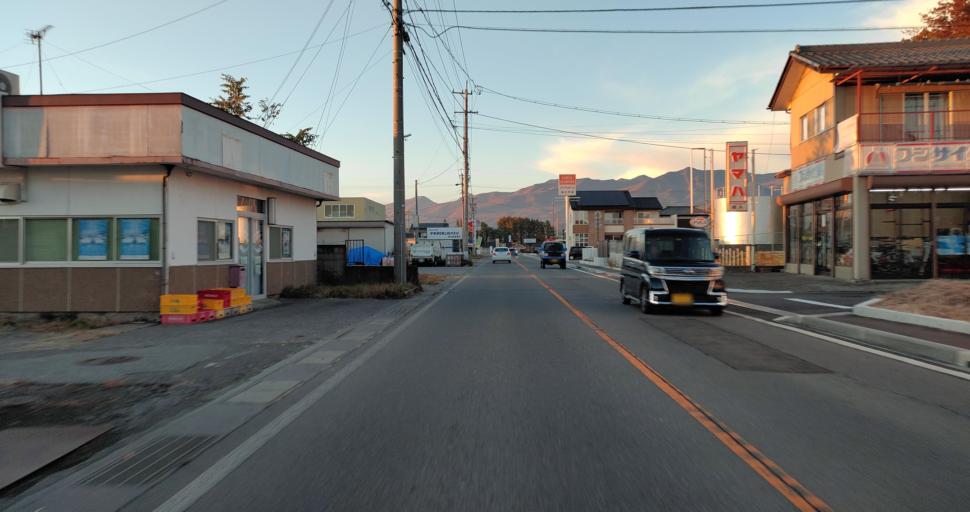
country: JP
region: Nagano
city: Komoro
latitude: 36.2914
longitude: 138.4599
